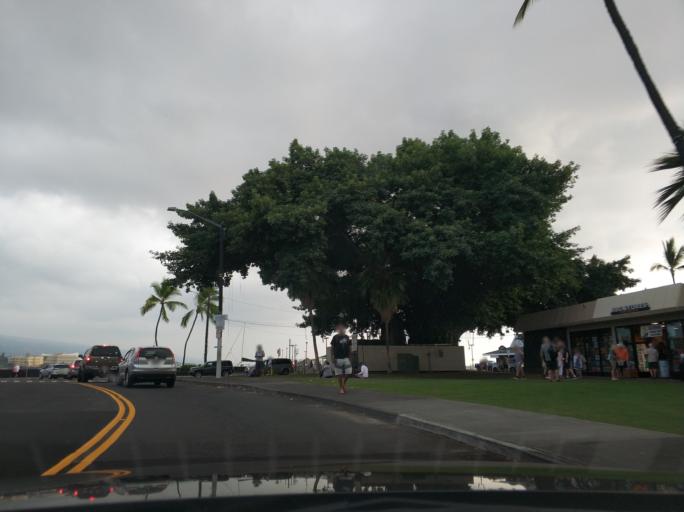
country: US
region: Hawaii
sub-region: Hawaii County
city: Kailua-Kona
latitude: 19.6407
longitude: -155.9970
